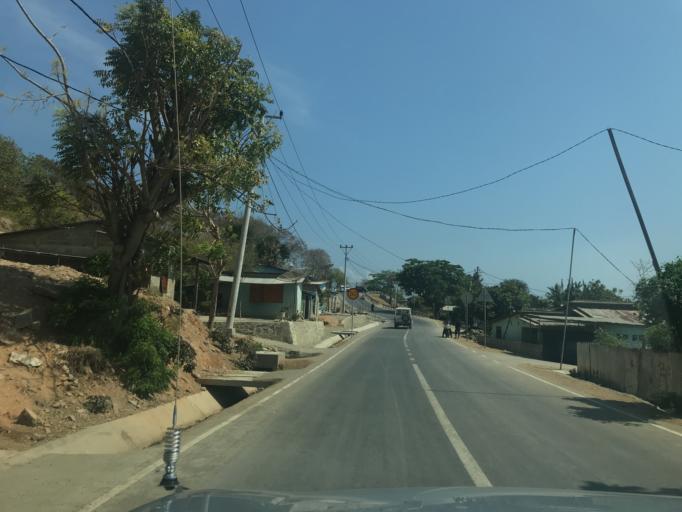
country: TL
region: Dili
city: Dili
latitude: -8.5607
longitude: 125.5227
